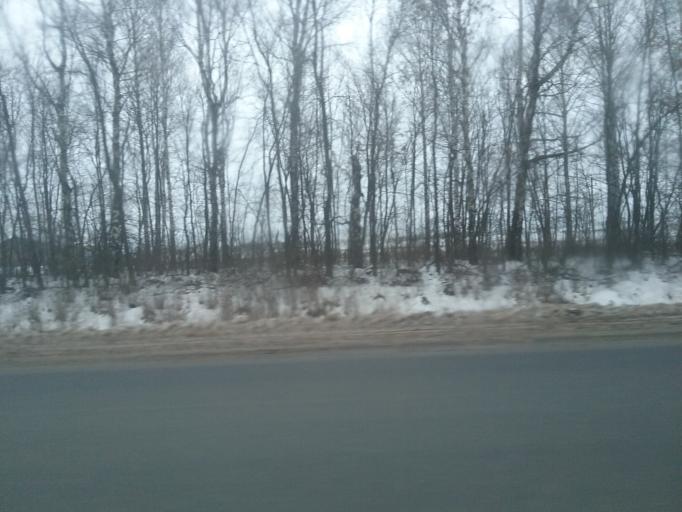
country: RU
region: Tula
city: Bolokhovo
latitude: 54.0405
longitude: 37.8675
